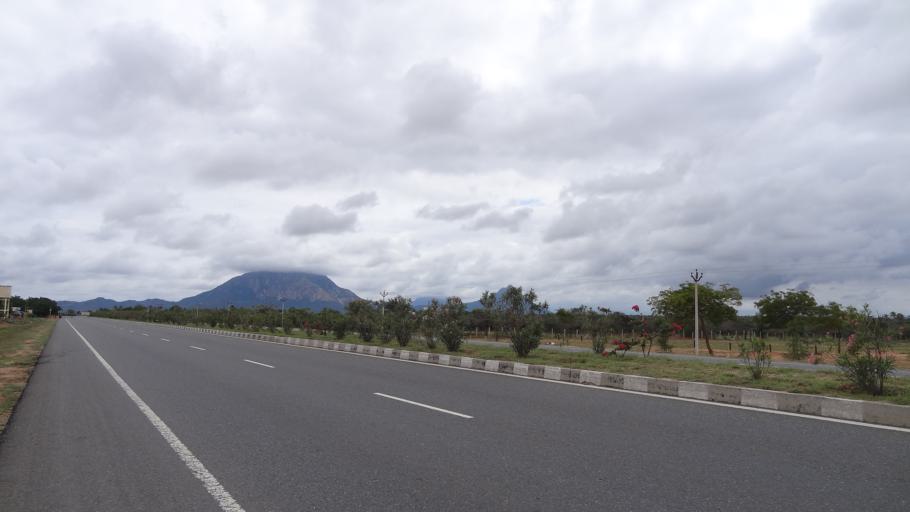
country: IN
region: Tamil Nadu
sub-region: Karur
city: Pallappatti
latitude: 10.7196
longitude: 77.9288
